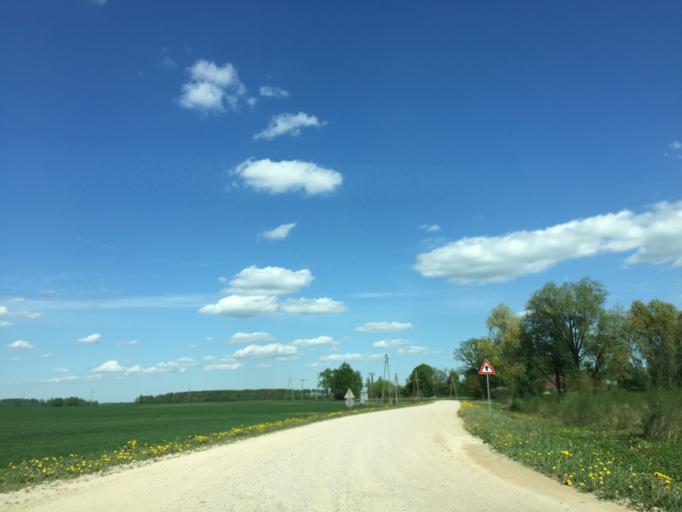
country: LV
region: Rundales
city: Pilsrundale
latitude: 56.3530
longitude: 23.9590
